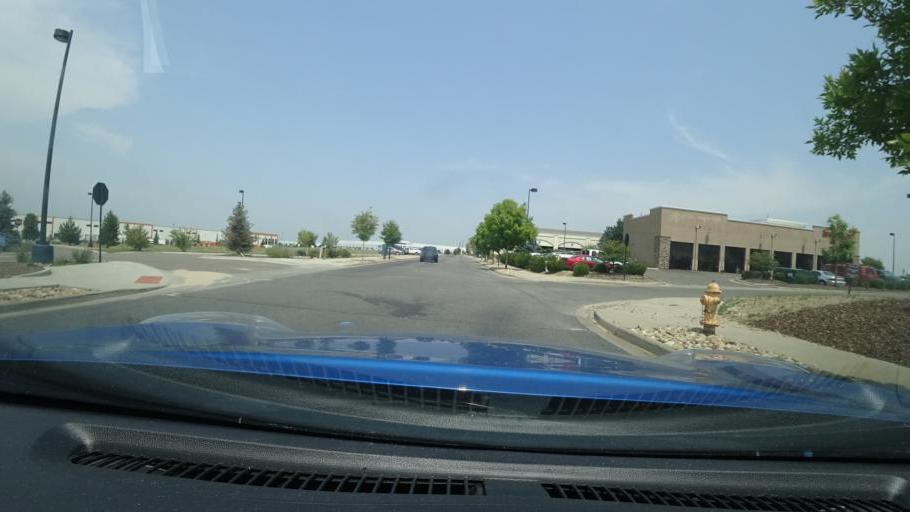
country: US
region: Colorado
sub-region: Adams County
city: Aurora
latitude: 39.7660
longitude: -104.7734
